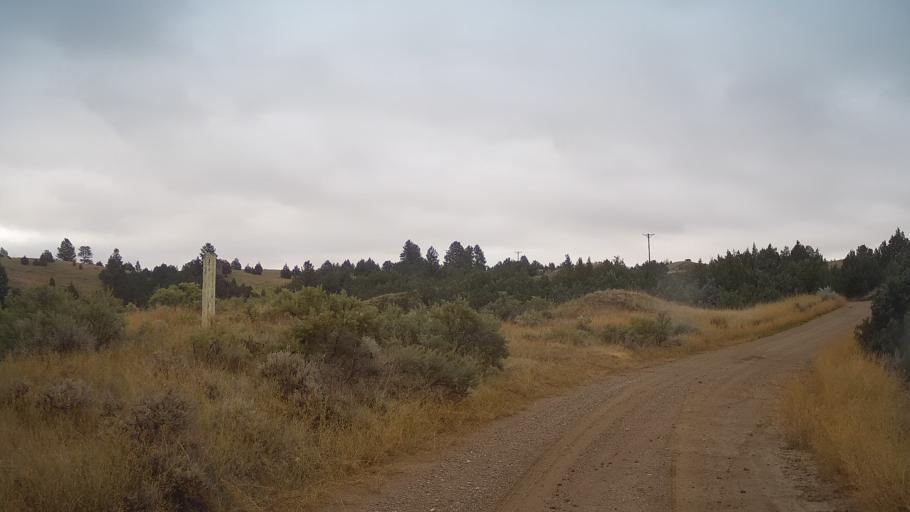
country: US
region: Montana
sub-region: Dawson County
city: Glendive
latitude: 47.0410
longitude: -104.6715
